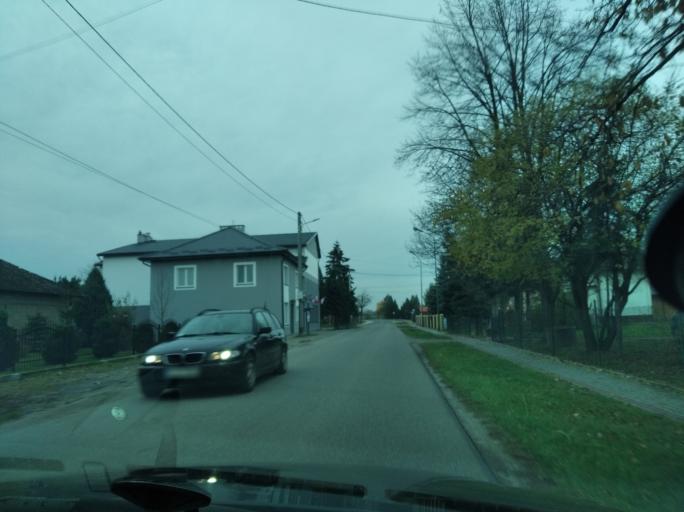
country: PL
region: Subcarpathian Voivodeship
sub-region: Powiat lancucki
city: Lancut
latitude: 50.0969
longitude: 22.2190
